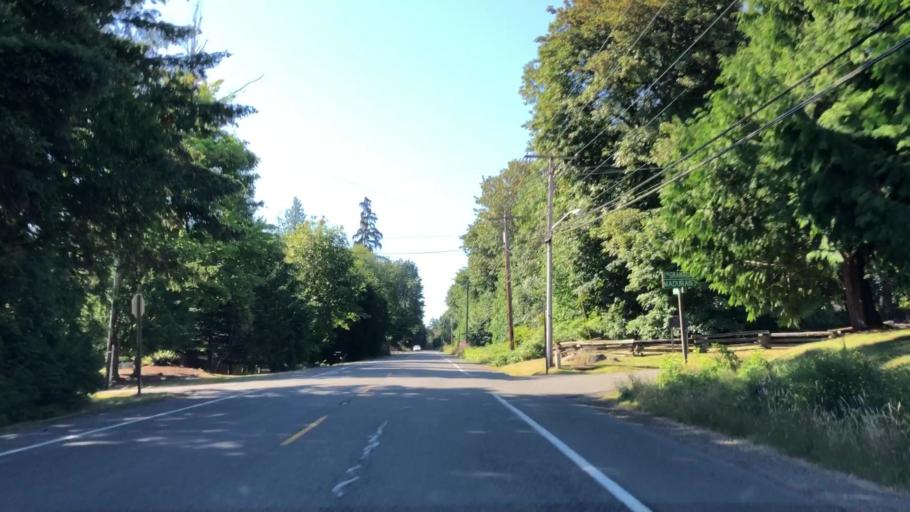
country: US
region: Washington
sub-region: Kitsap County
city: Kingston
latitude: 47.7858
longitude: -122.5027
